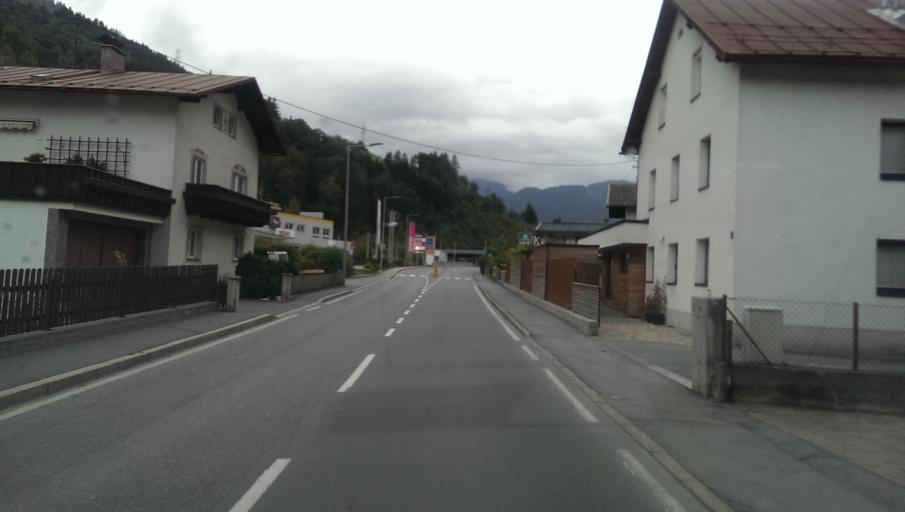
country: AT
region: Tyrol
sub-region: Politischer Bezirk Landeck
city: Stanz bei Landeck
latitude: 47.1414
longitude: 10.5510
